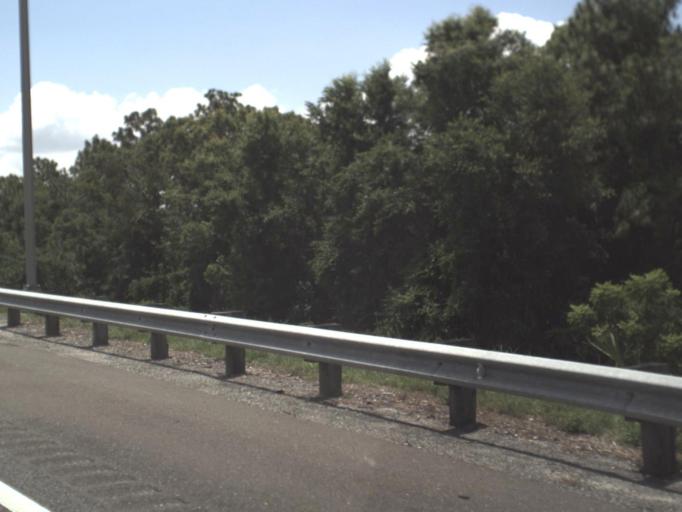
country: US
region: Florida
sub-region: Duval County
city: Jacksonville
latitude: 30.4404
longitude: -81.5894
